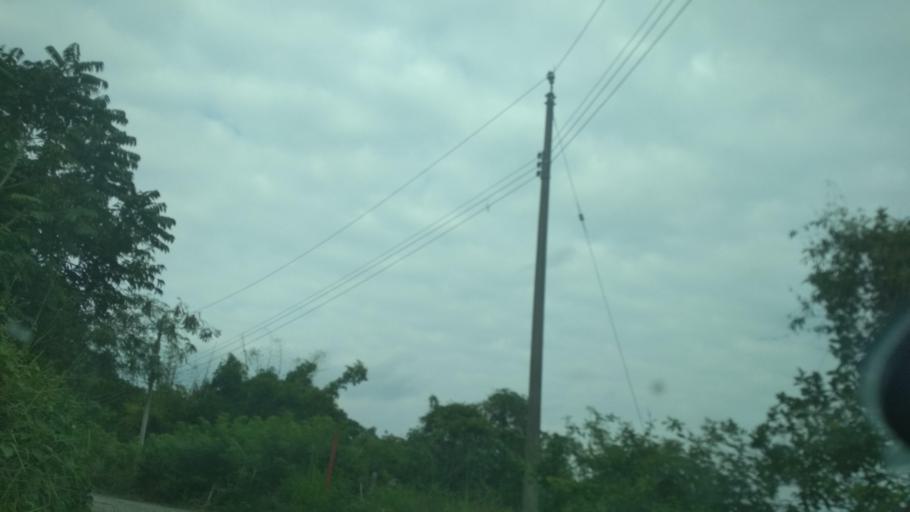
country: MX
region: Veracruz
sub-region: Poza Rica de Hidalgo
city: El Mollejon
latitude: 20.5218
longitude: -97.3790
